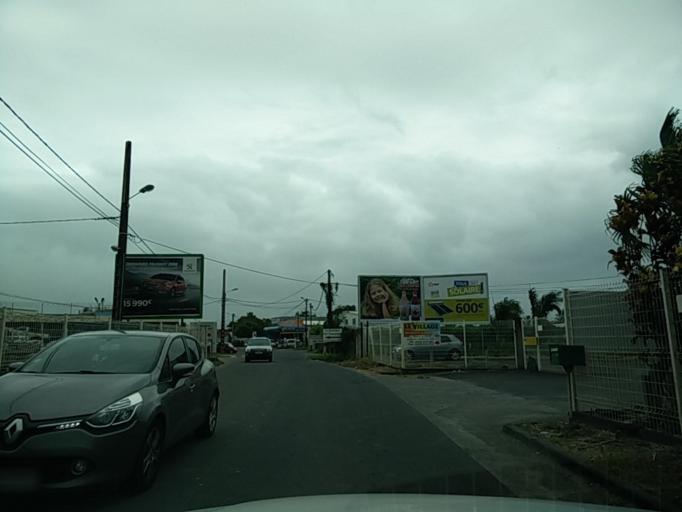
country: GP
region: Guadeloupe
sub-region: Guadeloupe
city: Pointe-a-Pitre
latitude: 16.2529
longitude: -61.5597
